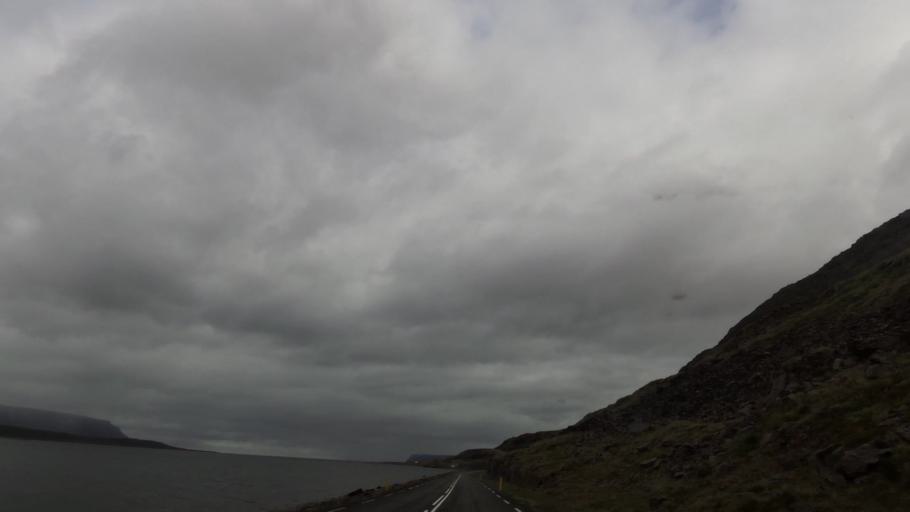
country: IS
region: Westfjords
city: Isafjoerdur
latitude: 65.9895
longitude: -22.7769
